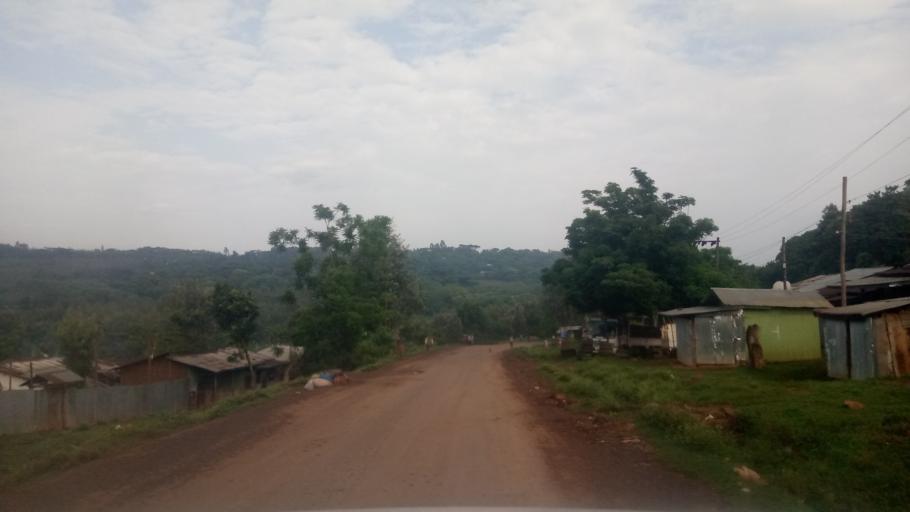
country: ET
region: Oromiya
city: Agaro
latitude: 7.8380
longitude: 36.6686
